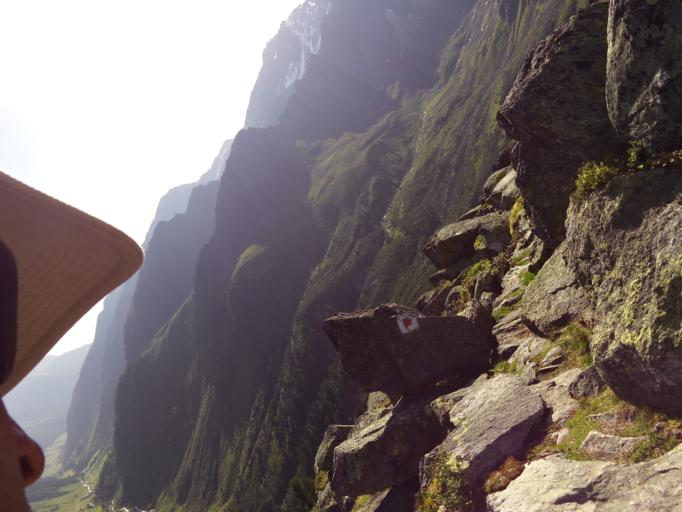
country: AT
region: Tyrol
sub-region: Politischer Bezirk Innsbruck Land
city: Gries im Sellrain
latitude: 47.0868
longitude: 11.1809
